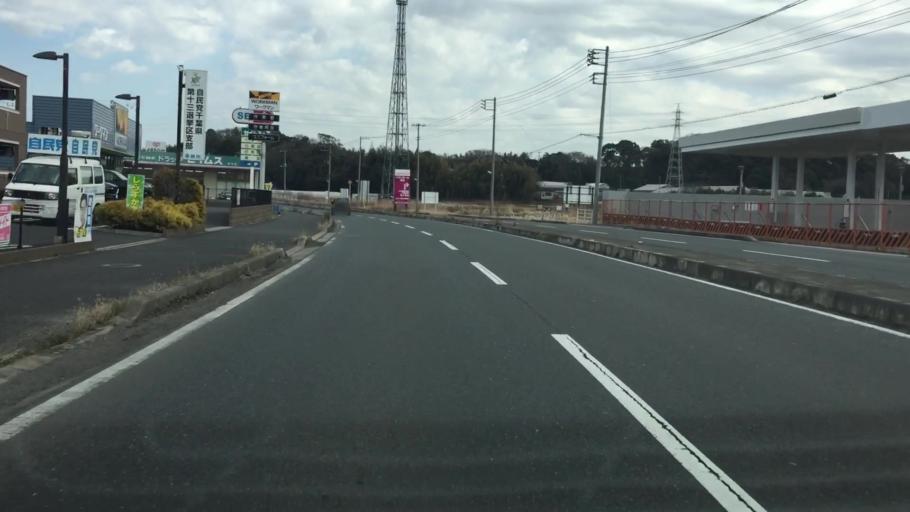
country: JP
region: Ibaraki
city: Ryugasaki
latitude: 35.8335
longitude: 140.1512
